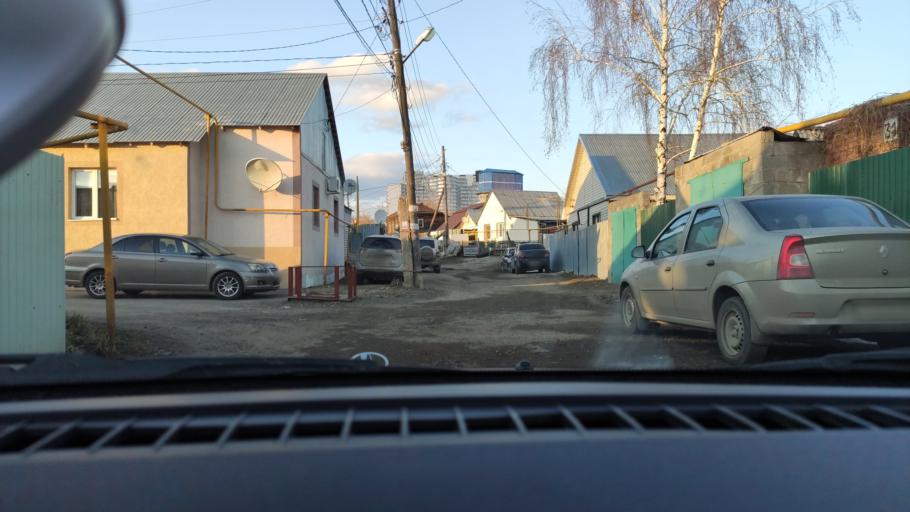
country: RU
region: Samara
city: Samara
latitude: 53.1819
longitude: 50.1305
